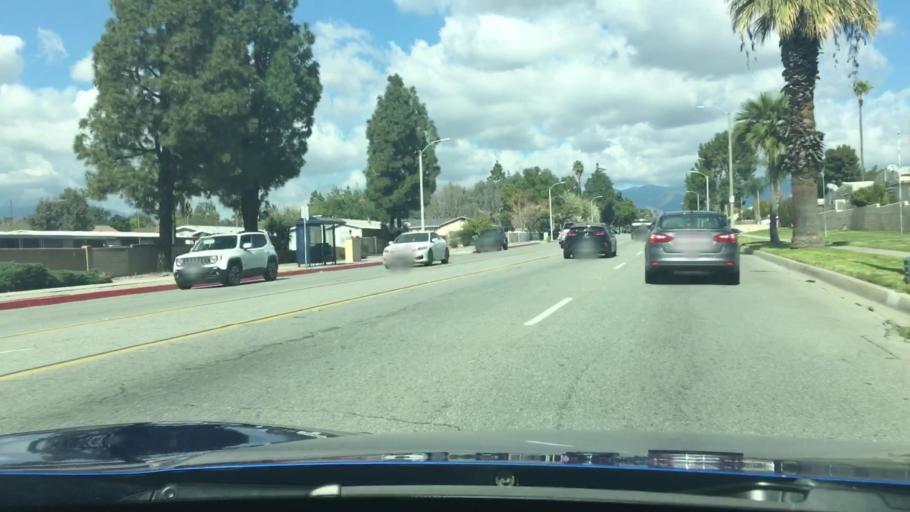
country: US
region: California
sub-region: San Bernardino County
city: Rialto
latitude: 34.0796
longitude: -117.3702
